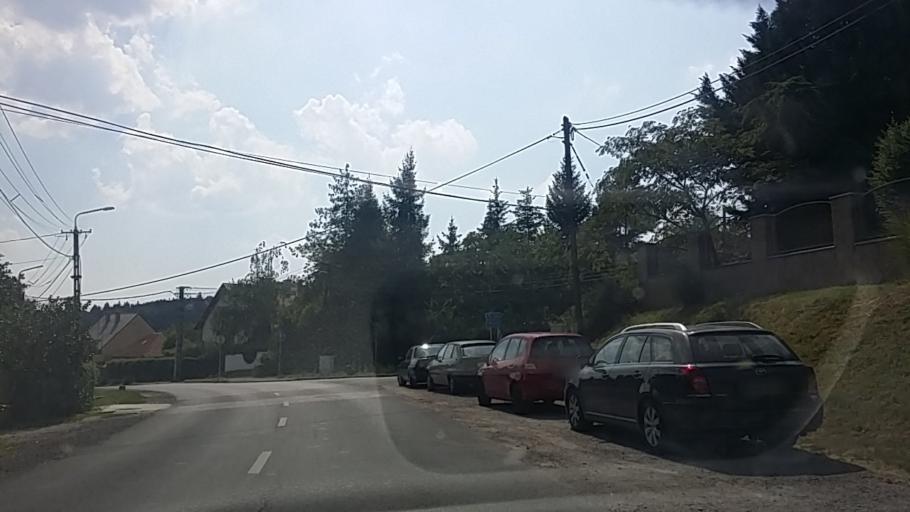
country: HU
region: Baranya
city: Pecs
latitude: 46.0773
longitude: 18.1876
